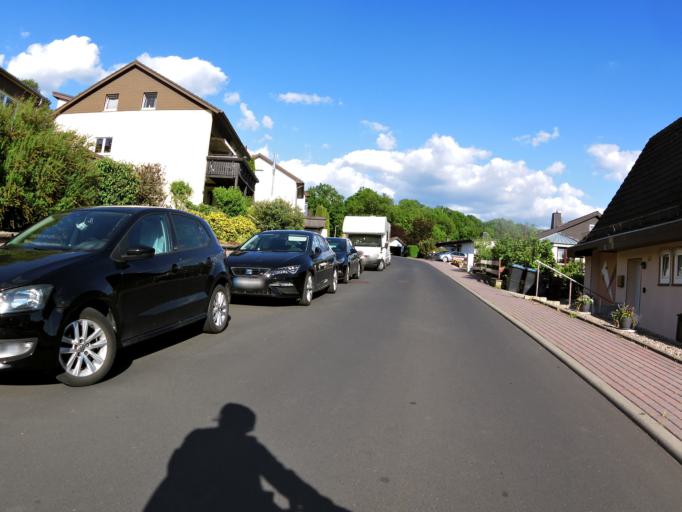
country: DE
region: Hesse
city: Philippsthal
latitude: 50.8373
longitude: 10.0149
